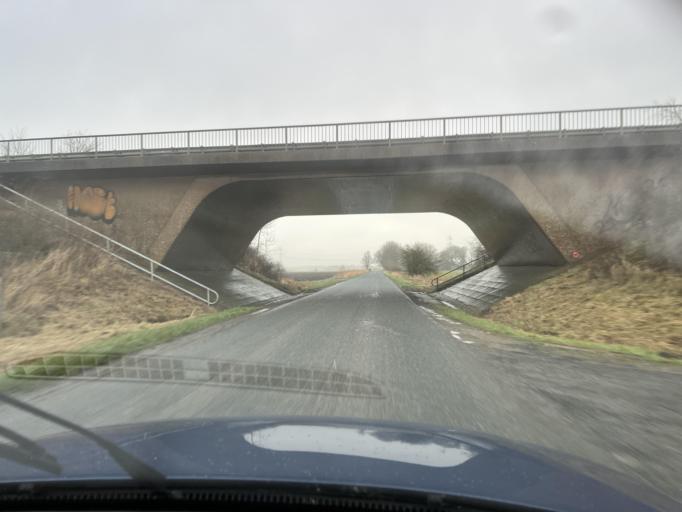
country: DE
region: Schleswig-Holstein
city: Lohe-Rickelshof
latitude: 54.2196
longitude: 9.0431
